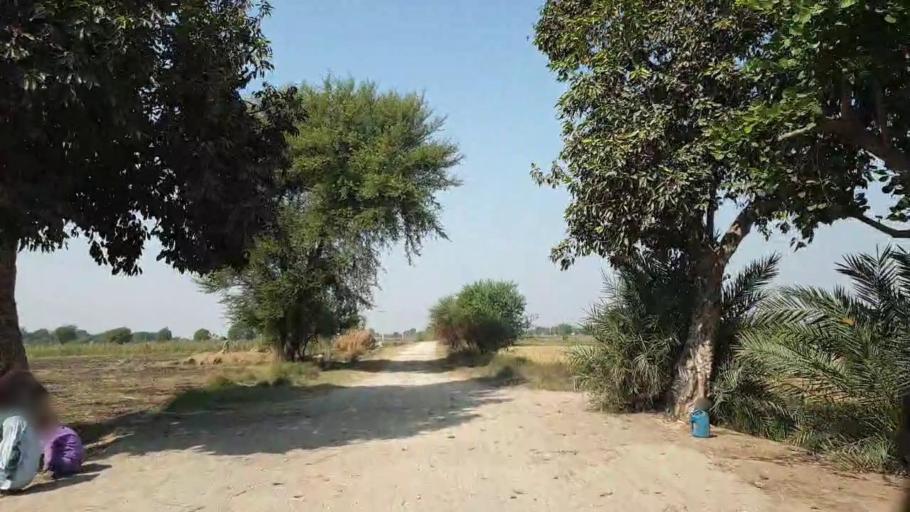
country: PK
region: Sindh
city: Tando Muhammad Khan
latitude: 25.0290
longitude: 68.4071
